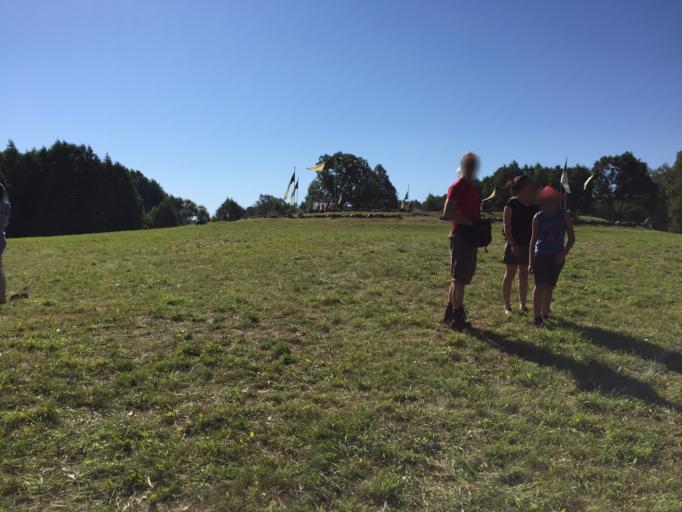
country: LT
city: Zarasai
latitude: 55.7893
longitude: 25.9600
